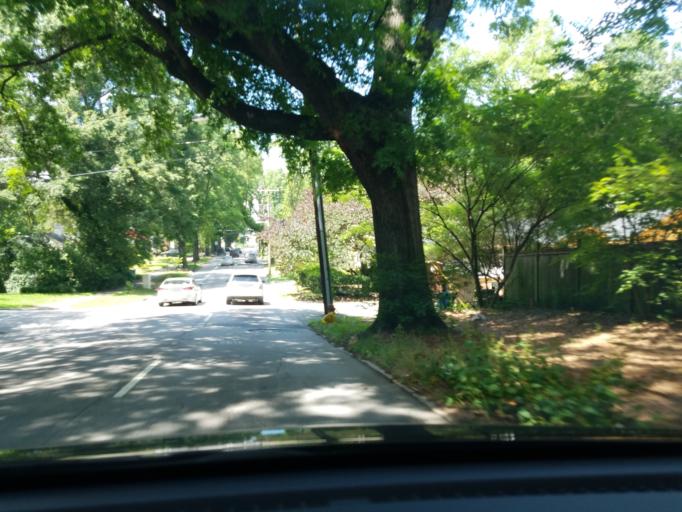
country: US
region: North Carolina
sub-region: Durham County
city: Durham
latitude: 36.0146
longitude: -78.9055
